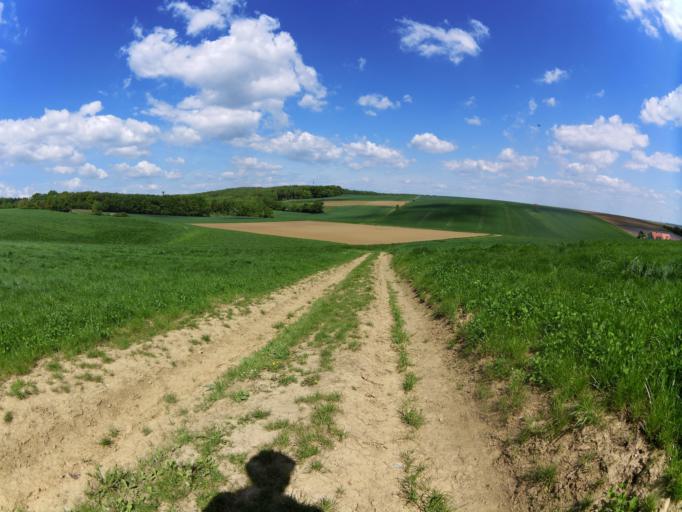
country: DE
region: Bavaria
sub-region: Regierungsbezirk Unterfranken
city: Unterpleichfeld
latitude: 49.8834
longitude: 10.0043
